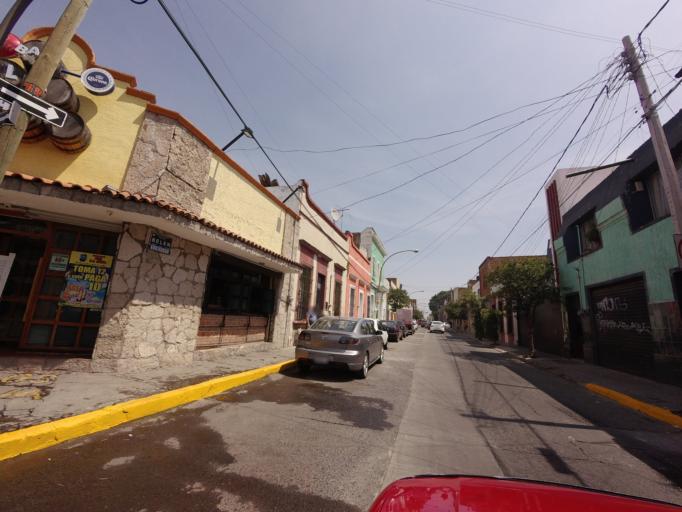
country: MX
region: Jalisco
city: Guadalajara
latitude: 20.6830
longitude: -103.3454
